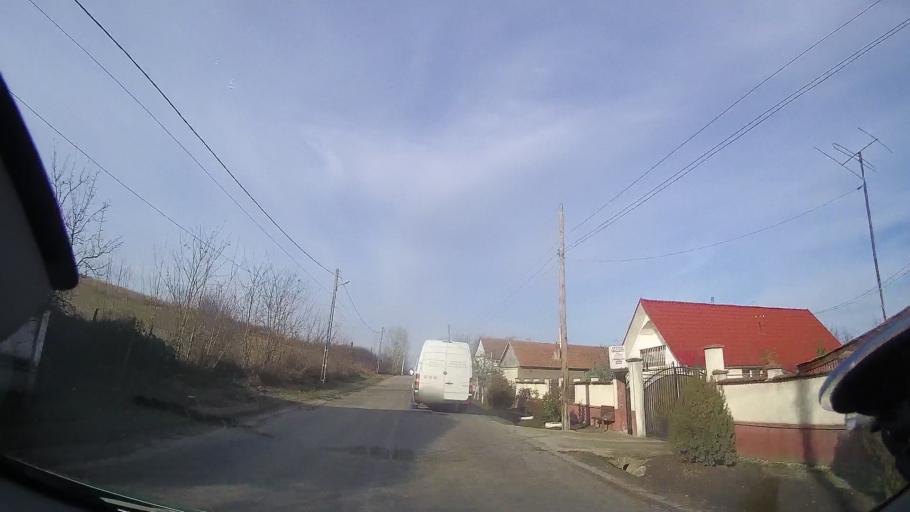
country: RO
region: Bihor
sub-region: Comuna Spinus
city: Spinus
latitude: 47.2022
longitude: 22.1833
